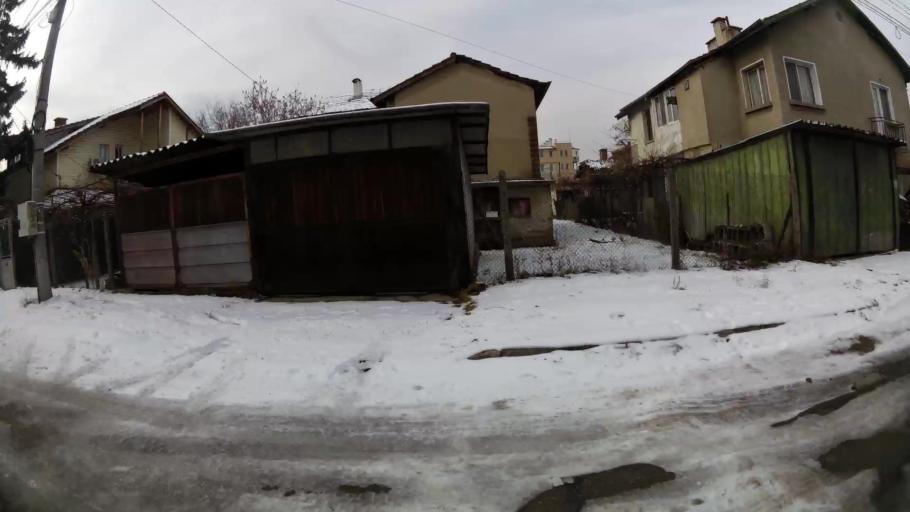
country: BG
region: Sofia-Capital
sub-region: Stolichna Obshtina
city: Sofia
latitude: 42.7089
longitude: 23.4045
